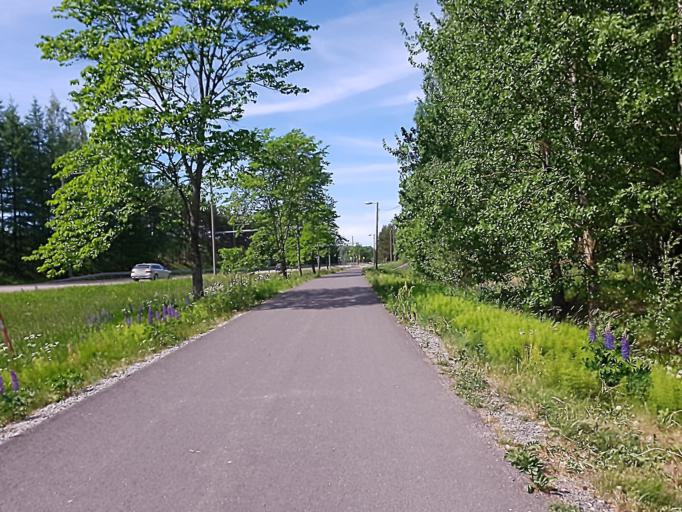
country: FI
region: Uusimaa
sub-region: Helsinki
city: Kilo
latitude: 60.3001
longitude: 24.8509
